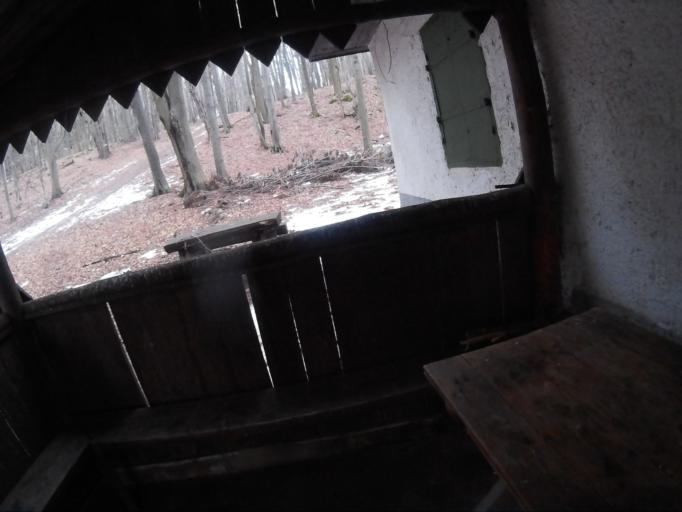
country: HU
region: Heves
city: Belapatfalva
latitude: 48.0492
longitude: 20.4090
